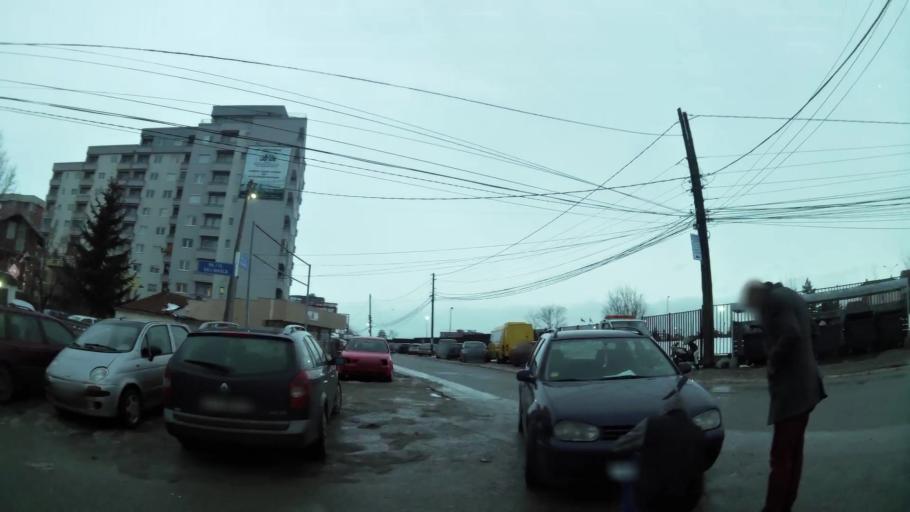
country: XK
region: Pristina
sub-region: Komuna e Prishtines
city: Pristina
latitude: 42.6589
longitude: 21.1778
